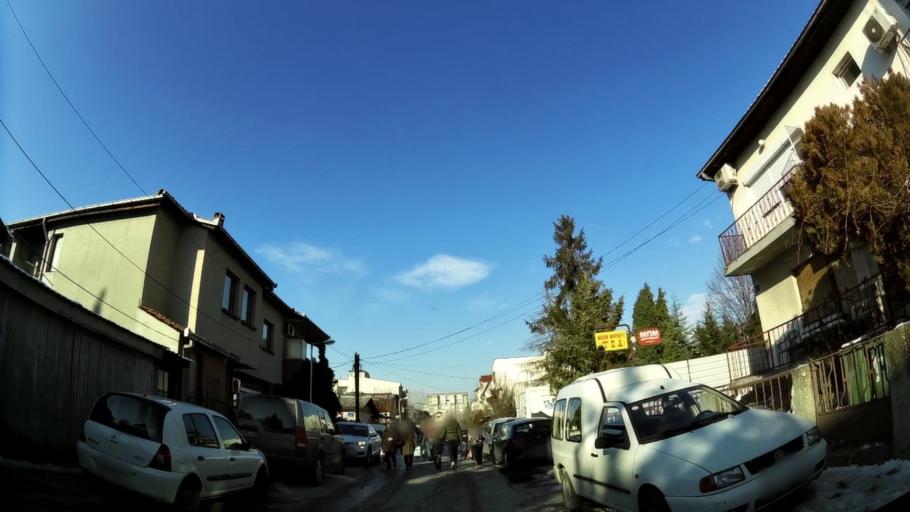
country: MK
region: Karpos
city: Skopje
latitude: 41.9993
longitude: 21.3945
